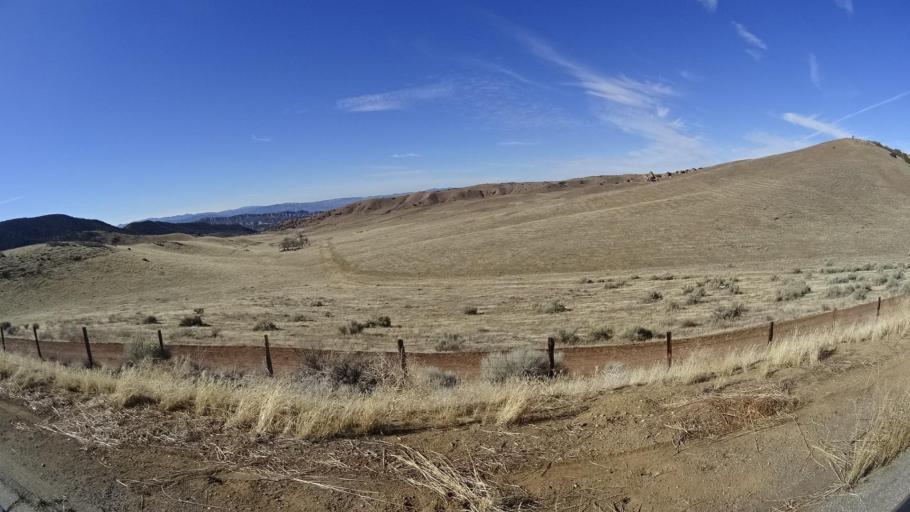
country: US
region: California
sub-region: Kern County
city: Maricopa
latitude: 34.8890
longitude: -119.3561
